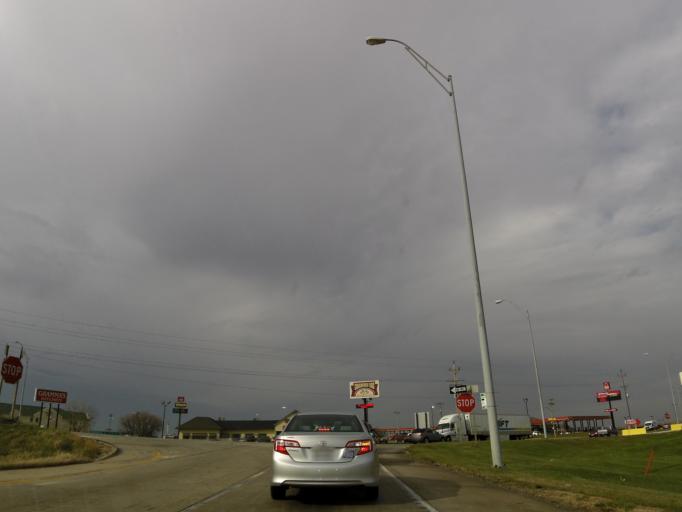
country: US
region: Iowa
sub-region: Scott County
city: Walcott
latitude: 41.6178
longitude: -90.7827
